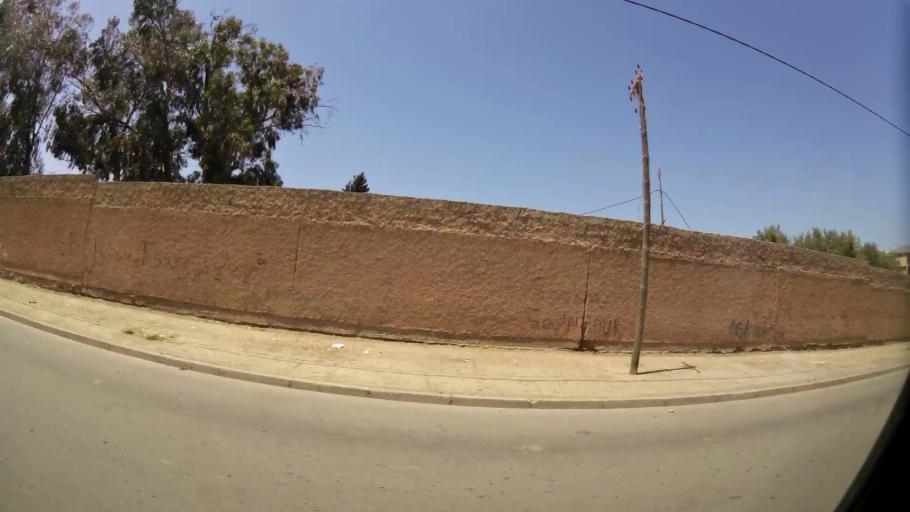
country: MA
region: Souss-Massa-Draa
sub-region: Inezgane-Ait Mellou
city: Inezgane
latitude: 30.3459
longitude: -9.4916
